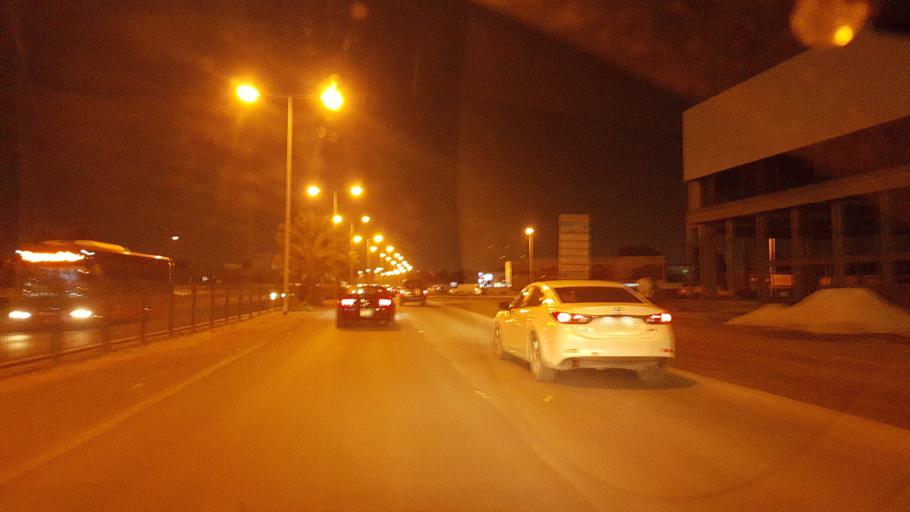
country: BH
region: Manama
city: Jidd Hafs
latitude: 26.2206
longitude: 50.5455
